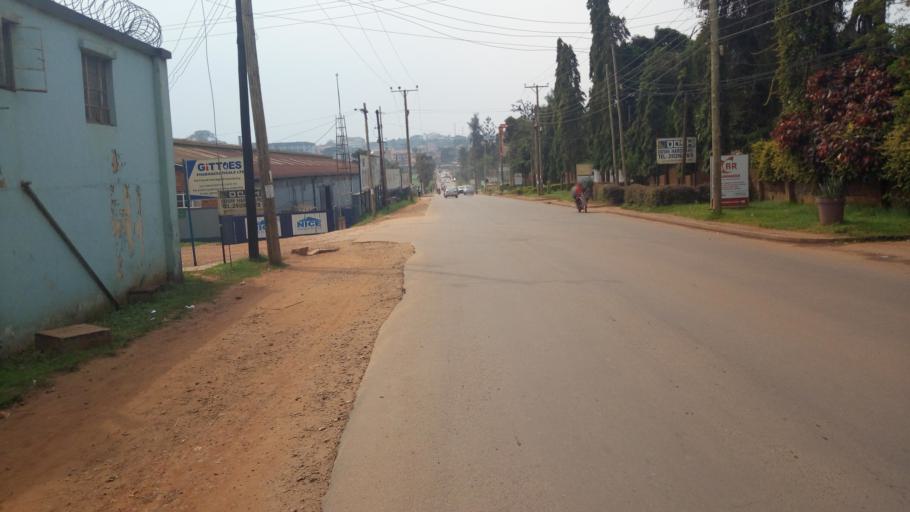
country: UG
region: Central Region
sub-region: Kampala District
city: Kampala
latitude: 0.3152
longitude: 32.6172
